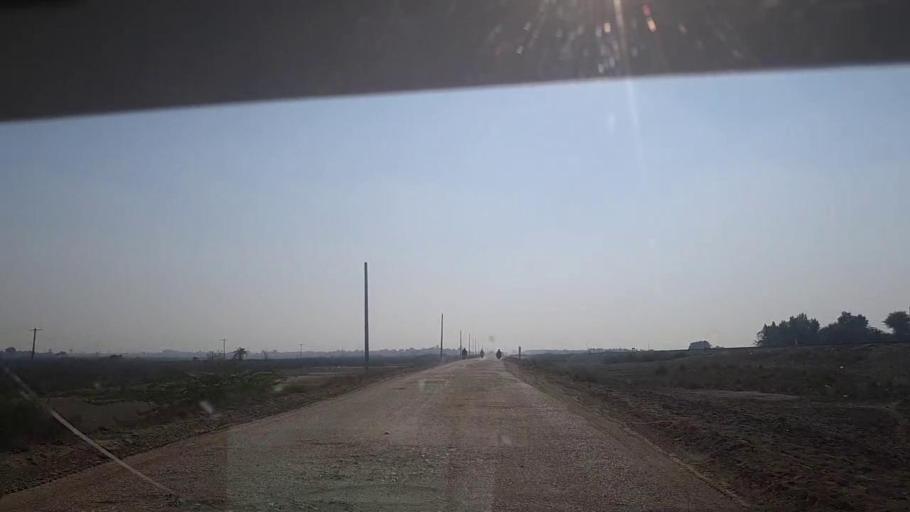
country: PK
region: Sindh
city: Gambat
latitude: 27.3594
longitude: 68.5543
